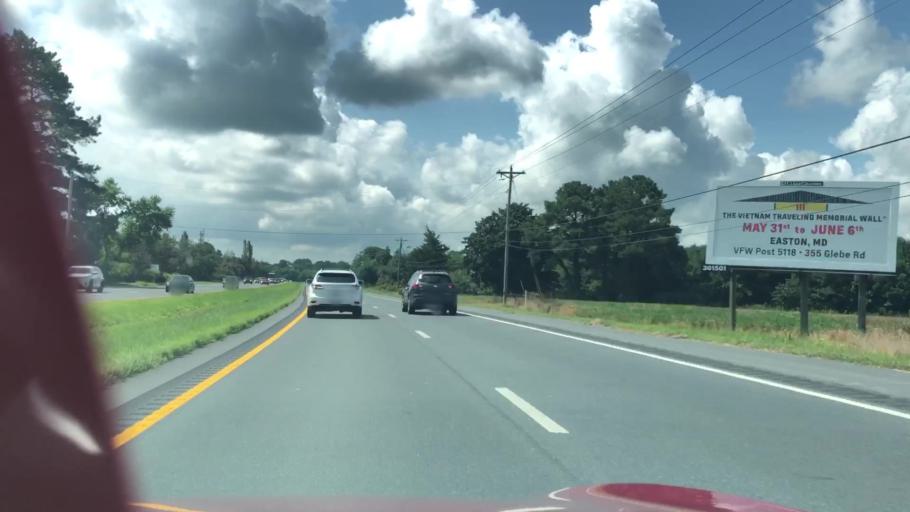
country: US
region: Virginia
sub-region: Accomack County
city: Accomac
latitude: 37.7783
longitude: -75.6112
